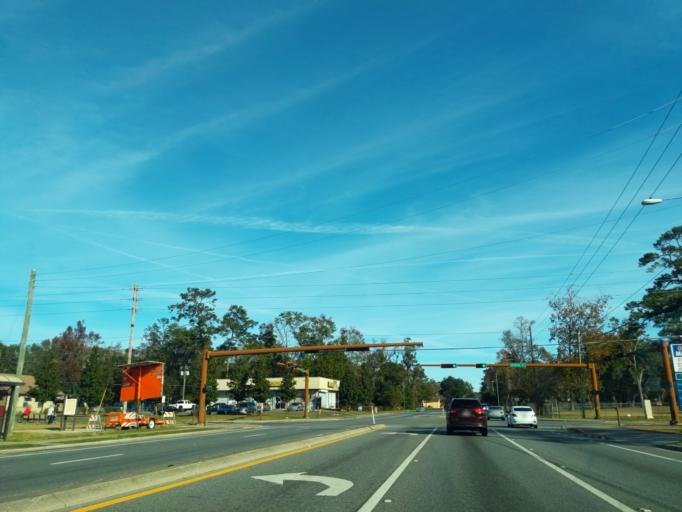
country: US
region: Florida
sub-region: Leon County
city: Tallahassee
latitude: 30.4126
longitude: -84.2777
